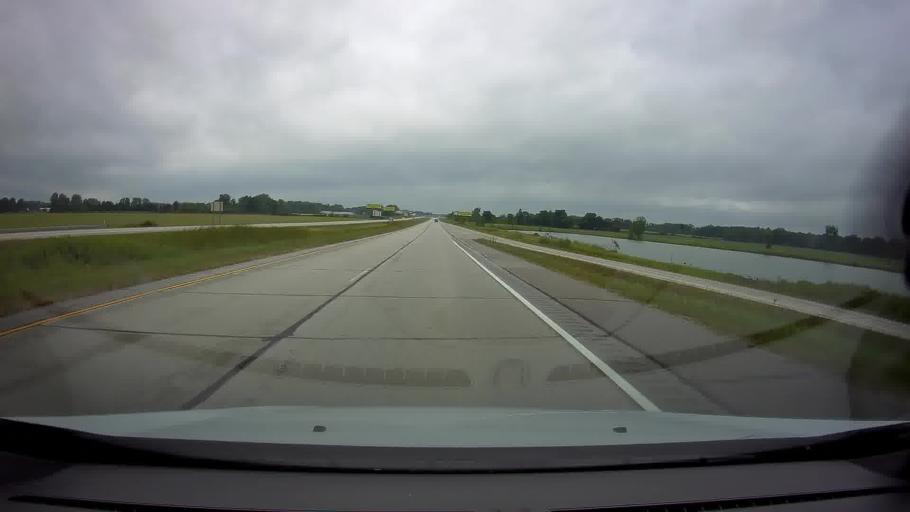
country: US
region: Wisconsin
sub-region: Brown County
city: Pulaski
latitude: 44.5979
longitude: -88.2243
